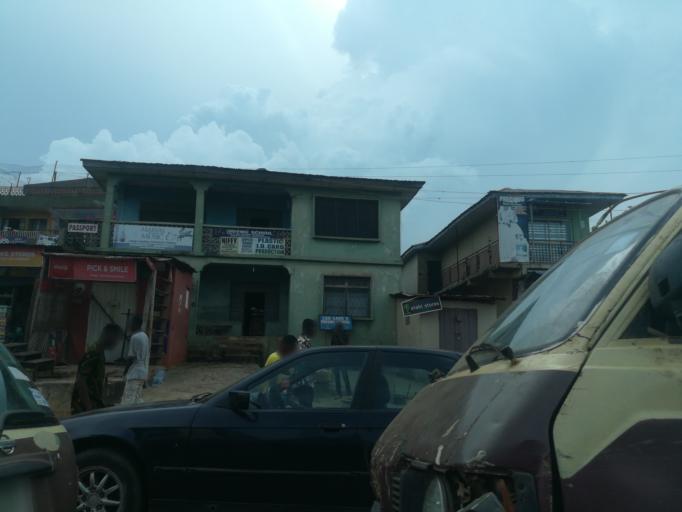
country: NG
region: Oyo
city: Ibadan
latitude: 7.4249
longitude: 3.8972
